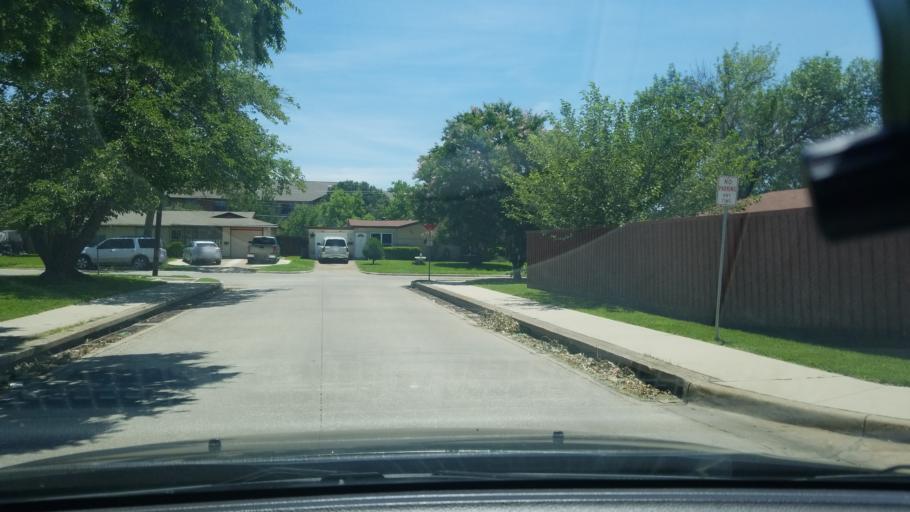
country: US
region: Texas
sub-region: Dallas County
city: Mesquite
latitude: 32.7738
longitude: -96.6111
